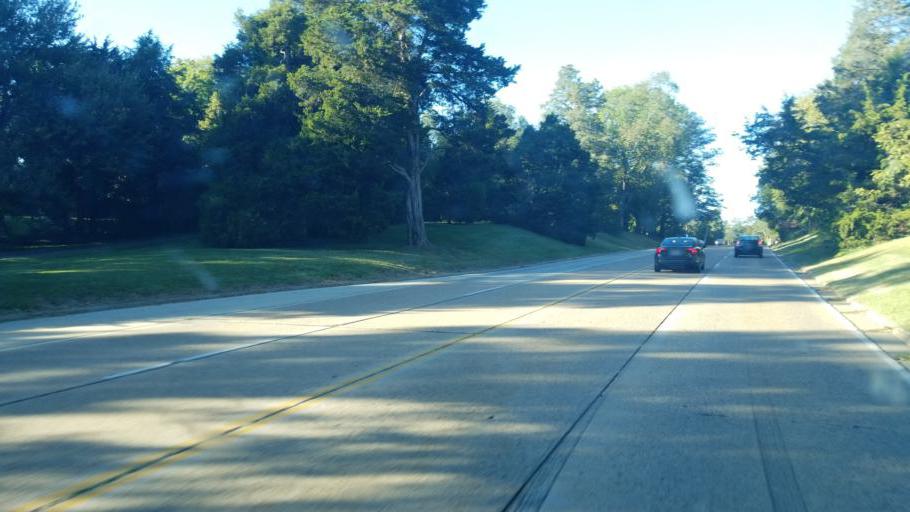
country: US
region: Virginia
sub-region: Fairfax County
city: Fort Hunt
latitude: 38.7378
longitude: -77.0487
